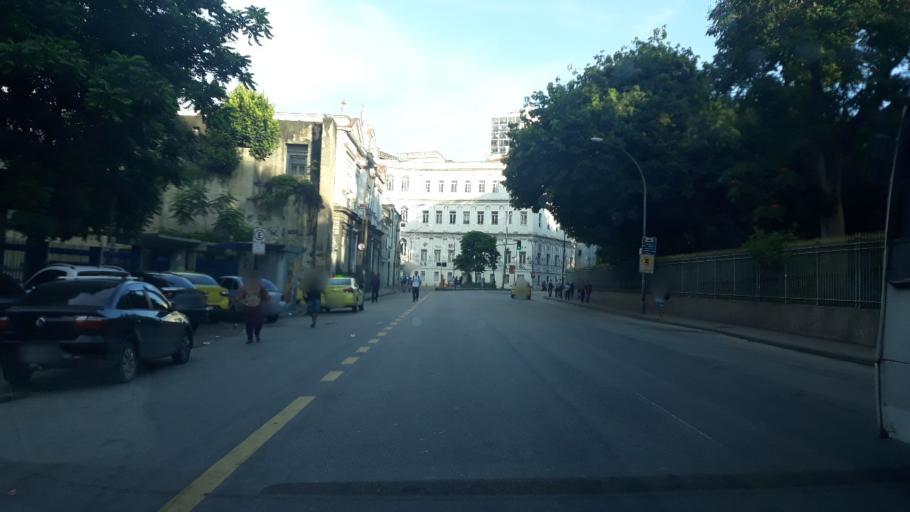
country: BR
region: Rio de Janeiro
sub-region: Rio De Janeiro
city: Rio de Janeiro
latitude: -22.9082
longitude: -43.1896
